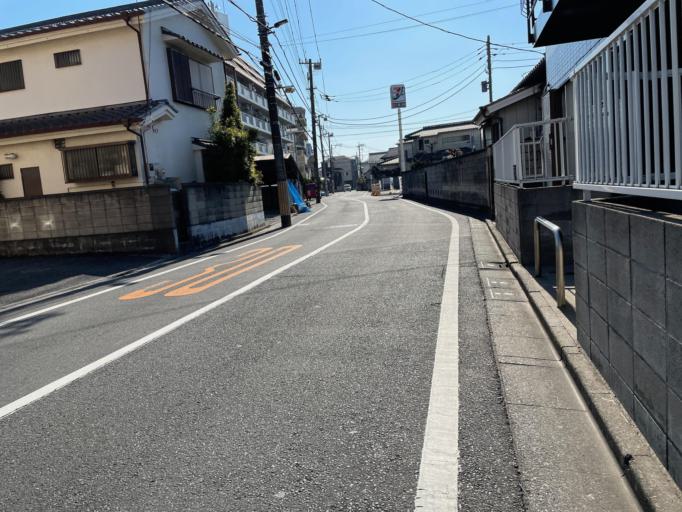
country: JP
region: Saitama
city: Soka
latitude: 35.7930
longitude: 139.7826
